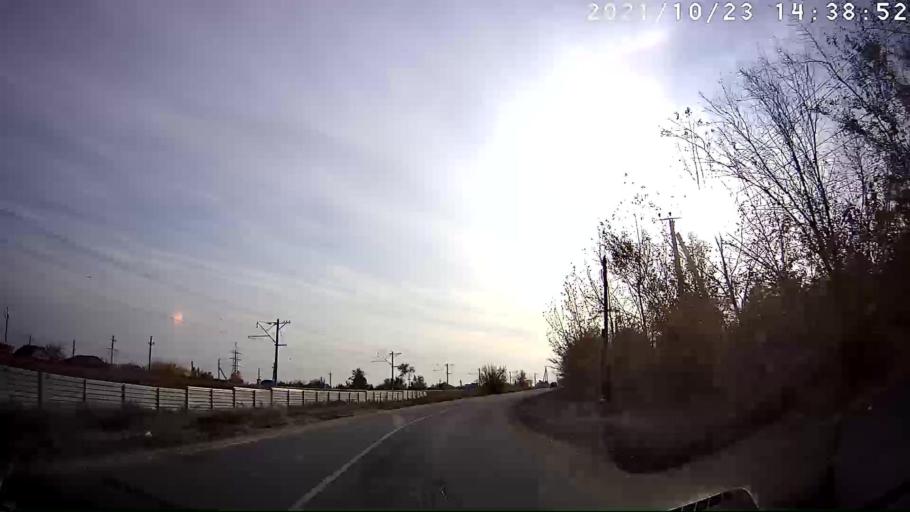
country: RU
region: Volgograd
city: Krasnoslobodsk
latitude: 48.4890
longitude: 44.5486
